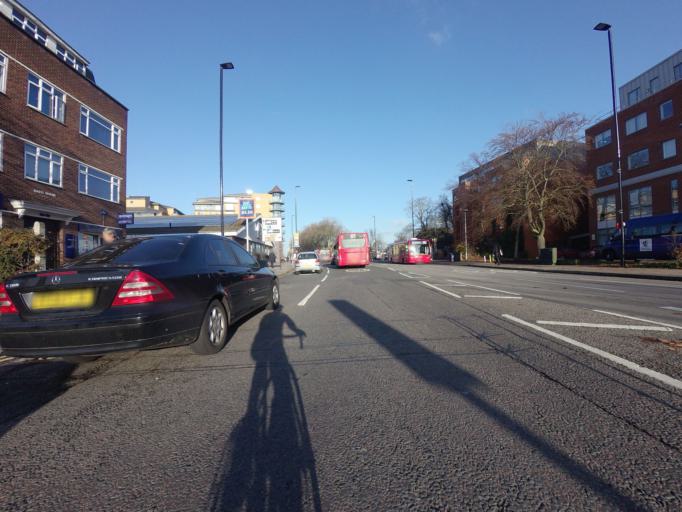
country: GB
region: England
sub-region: Greater London
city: Feltham
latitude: 51.4433
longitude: -0.4118
